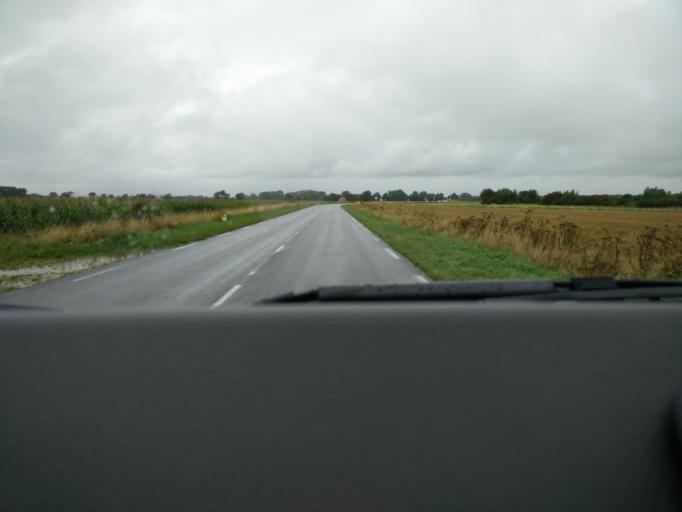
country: FR
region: Picardie
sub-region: Departement de la Somme
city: Le Crotoy
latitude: 50.2343
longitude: 1.6443
